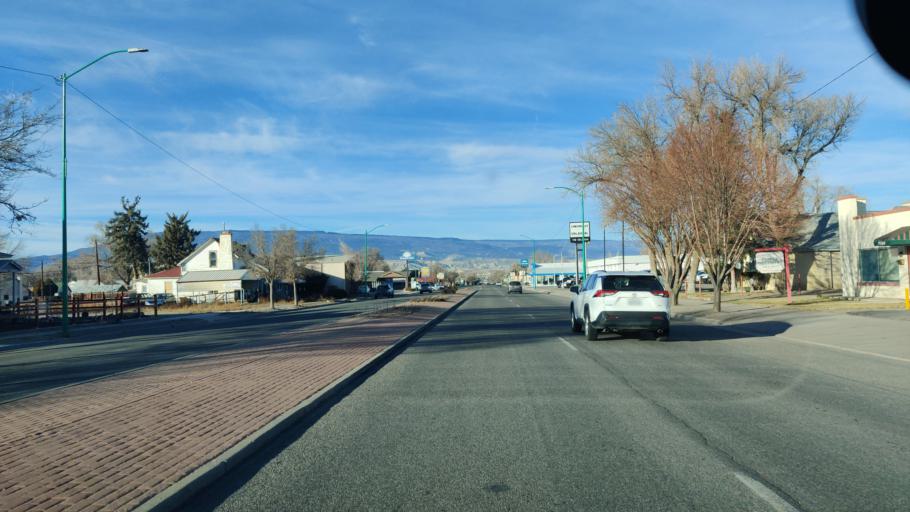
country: US
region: Colorado
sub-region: Delta County
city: Delta
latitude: 38.7334
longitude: -108.0707
